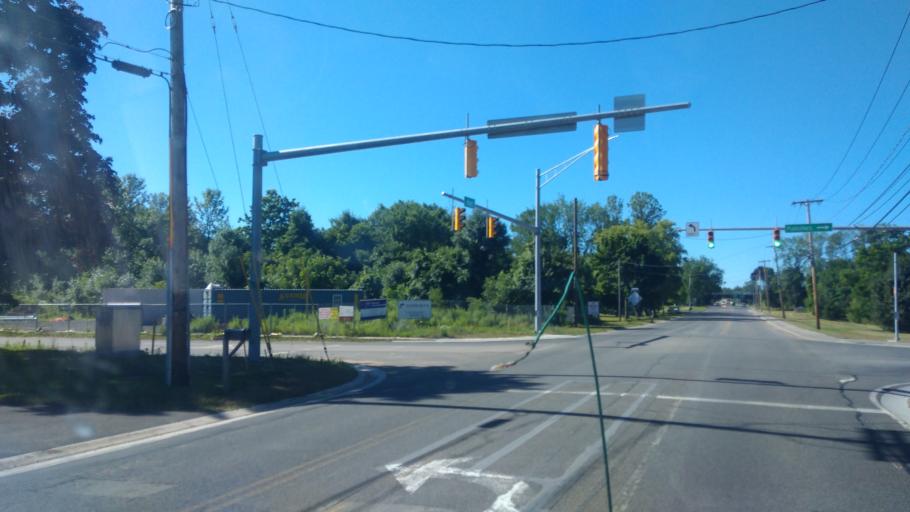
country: US
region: New York
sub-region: Monroe County
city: Webster
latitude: 43.2184
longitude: -77.4613
